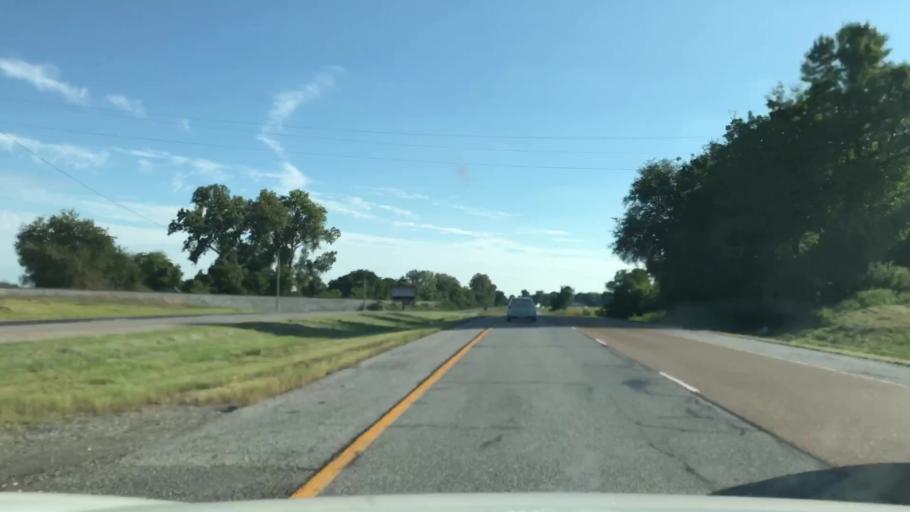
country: US
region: Illinois
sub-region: Madison County
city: Mitchell
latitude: 38.7878
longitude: -90.1061
